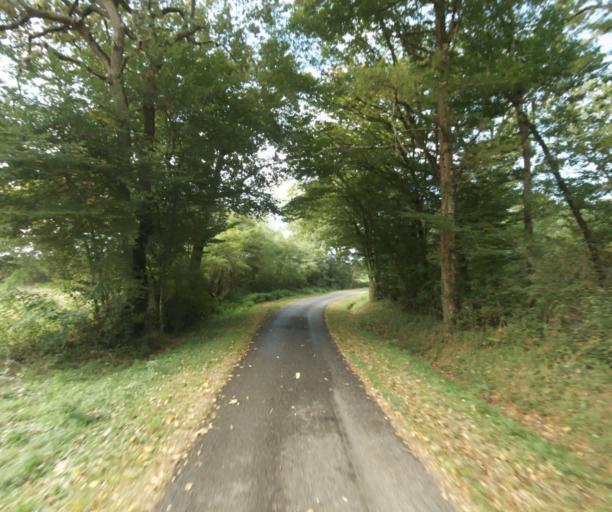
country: FR
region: Aquitaine
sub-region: Departement des Landes
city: Villeneuve-de-Marsan
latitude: 43.9074
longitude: -0.2302
